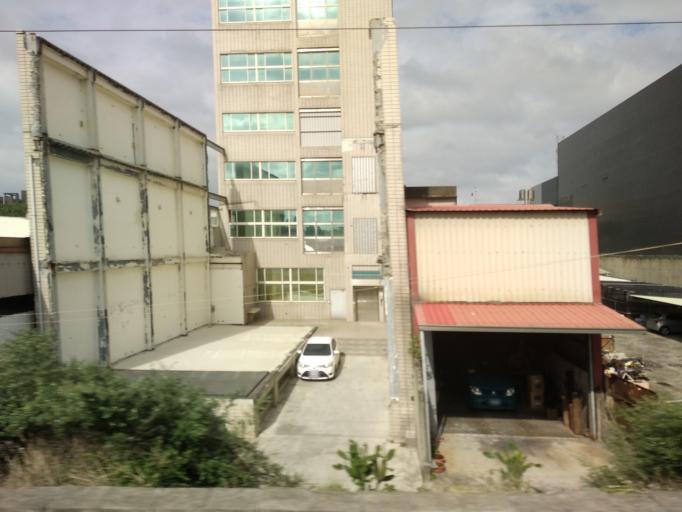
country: TW
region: Taiwan
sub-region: Hsinchu
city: Hsinchu
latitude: 24.8120
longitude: 120.9901
